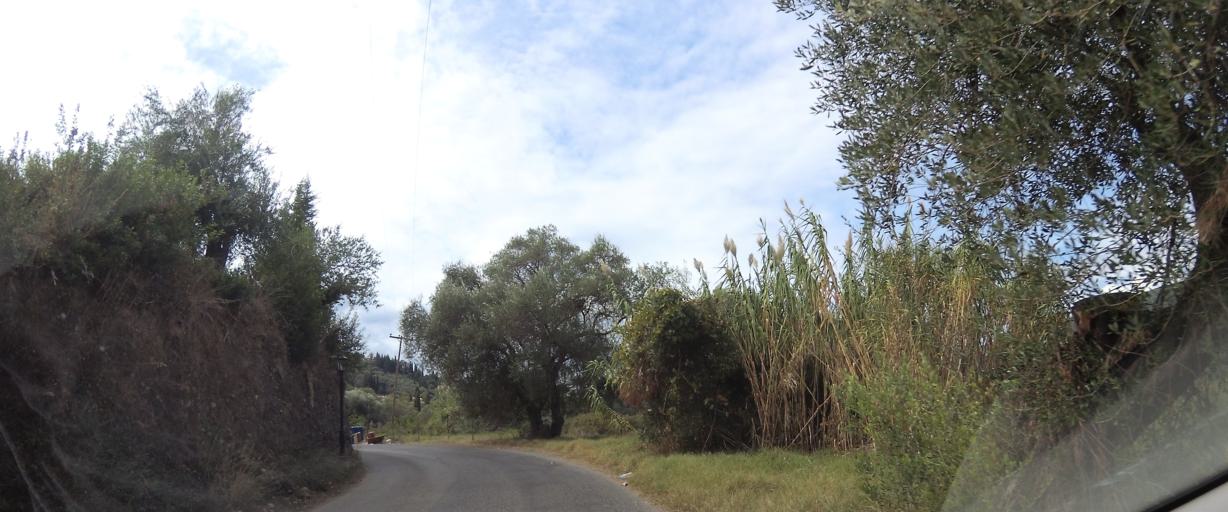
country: GR
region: Ionian Islands
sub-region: Nomos Kerkyras
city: Kontokali
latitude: 39.6918
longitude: 19.8203
